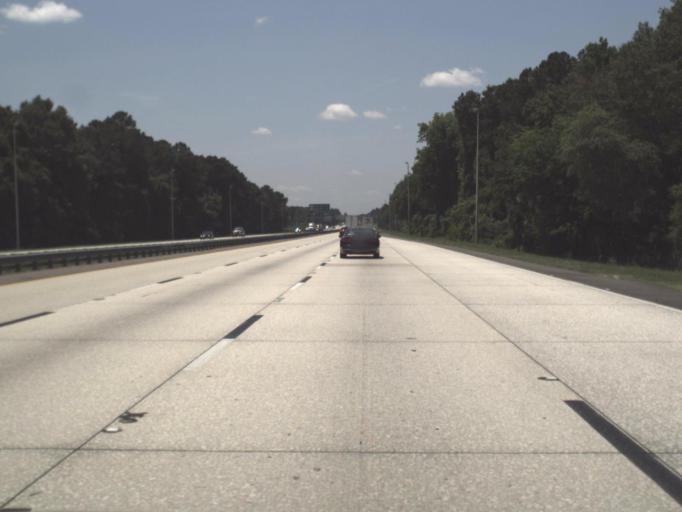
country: US
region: Florida
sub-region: Duval County
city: Jacksonville
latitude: 30.4533
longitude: -81.6514
